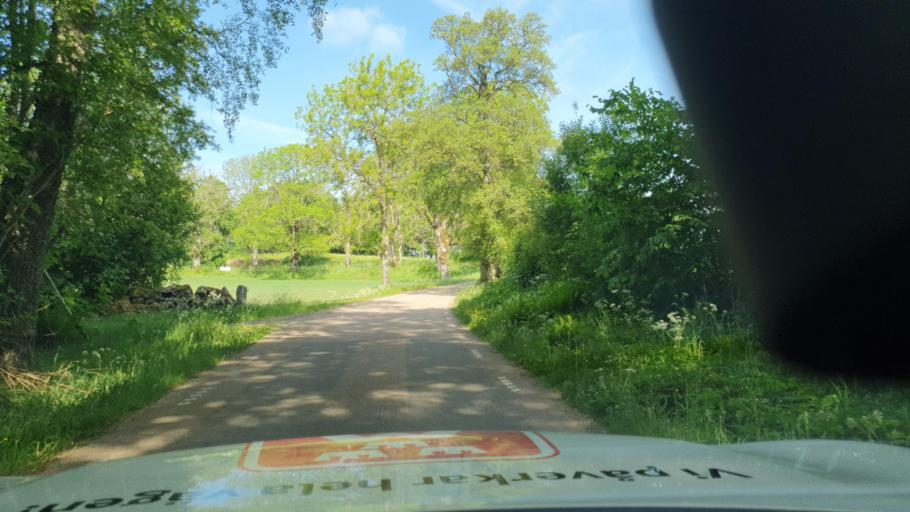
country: SE
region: Vaestra Goetaland
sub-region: Herrljunga Kommun
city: Herrljunga
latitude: 57.9253
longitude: 13.1263
